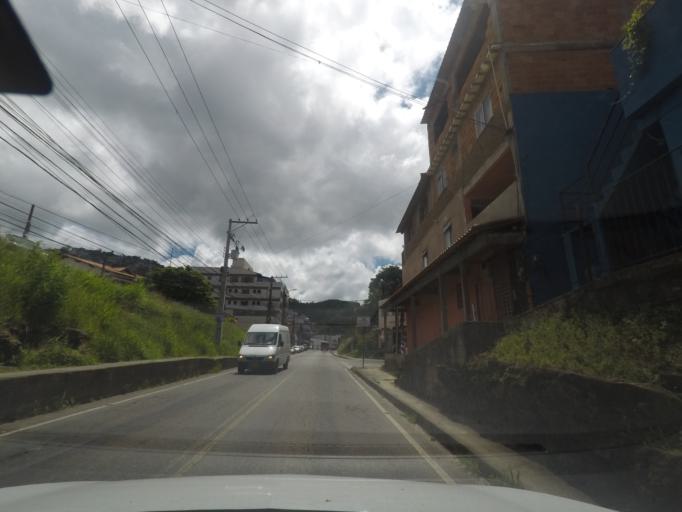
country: BR
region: Rio de Janeiro
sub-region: Teresopolis
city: Teresopolis
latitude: -22.4005
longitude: -42.9764
